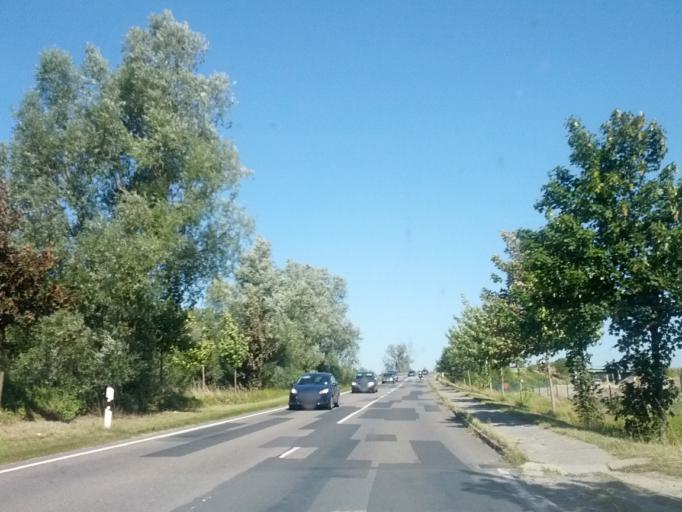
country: DE
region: Mecklenburg-Vorpommern
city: Sagard
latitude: 54.4849
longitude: 13.5774
